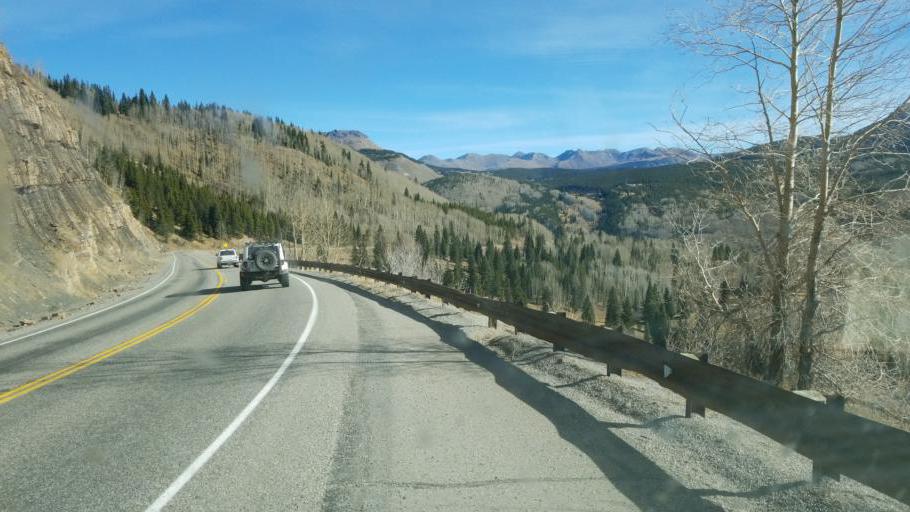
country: US
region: Colorado
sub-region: San Juan County
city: Silverton
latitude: 37.7084
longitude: -107.7655
